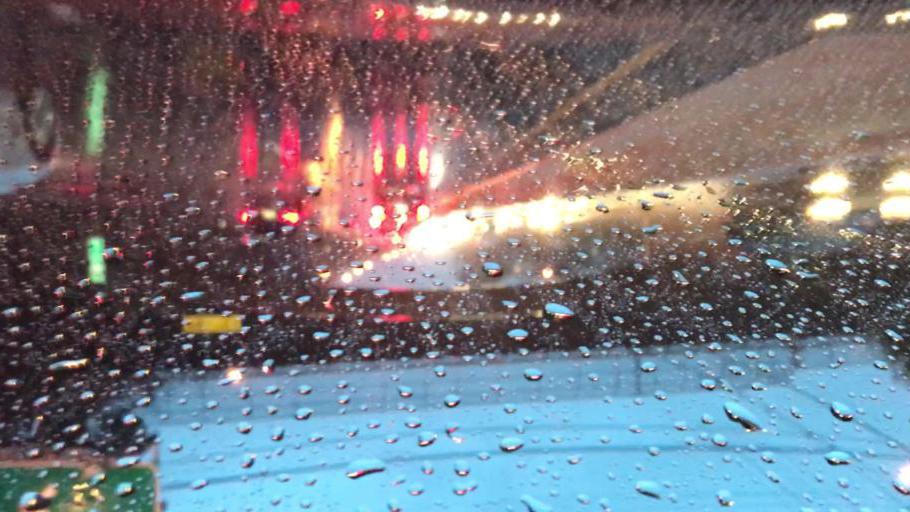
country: US
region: New Jersey
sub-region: Bergen County
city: Fair Lawn
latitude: 40.9375
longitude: -74.1254
